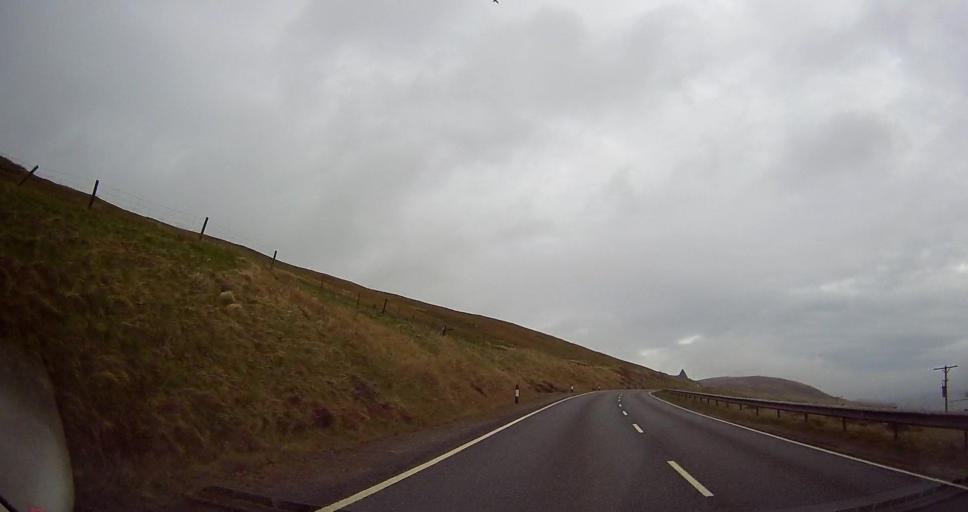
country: GB
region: Scotland
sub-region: Shetland Islands
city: Lerwick
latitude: 60.1665
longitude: -1.2277
